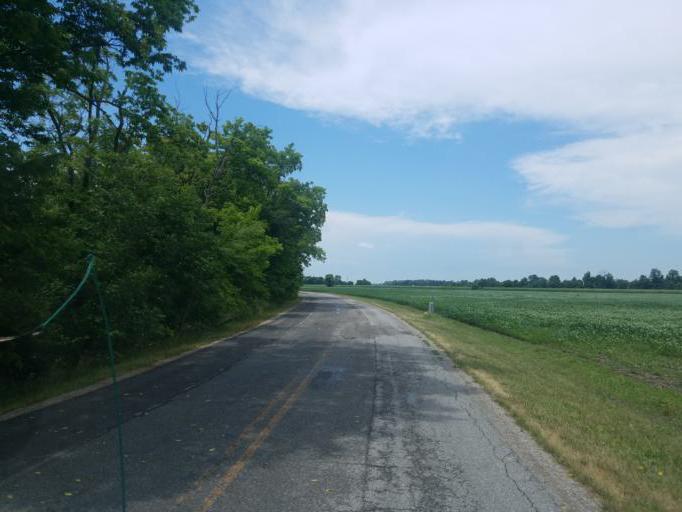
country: US
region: Ohio
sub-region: Paulding County
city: Antwerp
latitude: 41.1986
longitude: -84.7395
